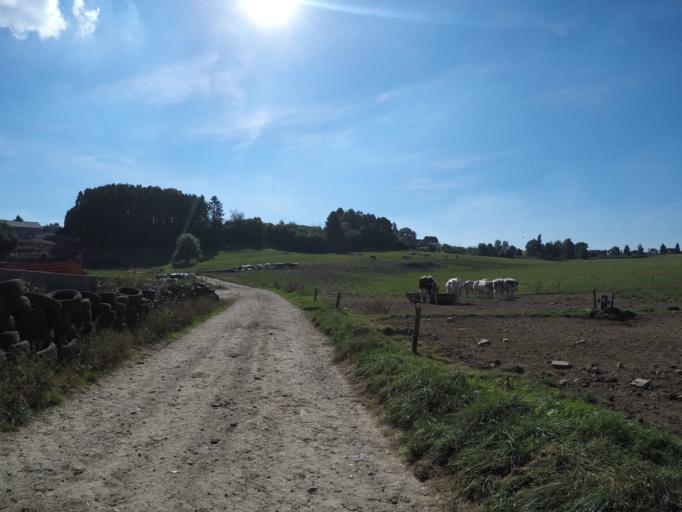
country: BE
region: Wallonia
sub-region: Province de Namur
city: Ciney
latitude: 50.3145
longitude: 5.0582
